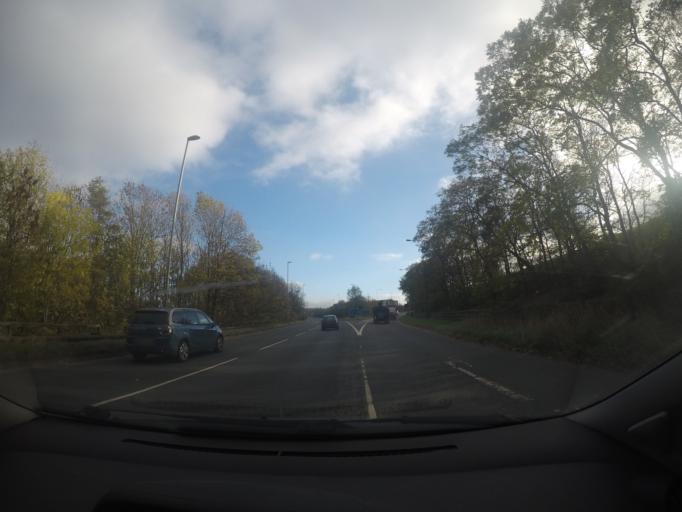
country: GB
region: England
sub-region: City and Borough of Leeds
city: Lofthouse
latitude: 53.7678
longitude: -1.5141
